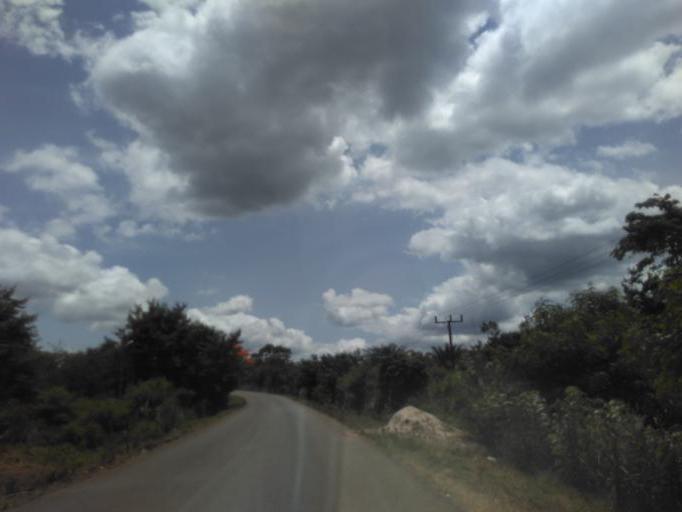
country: GH
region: Eastern
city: Koforidua
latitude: 6.1262
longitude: -0.1921
